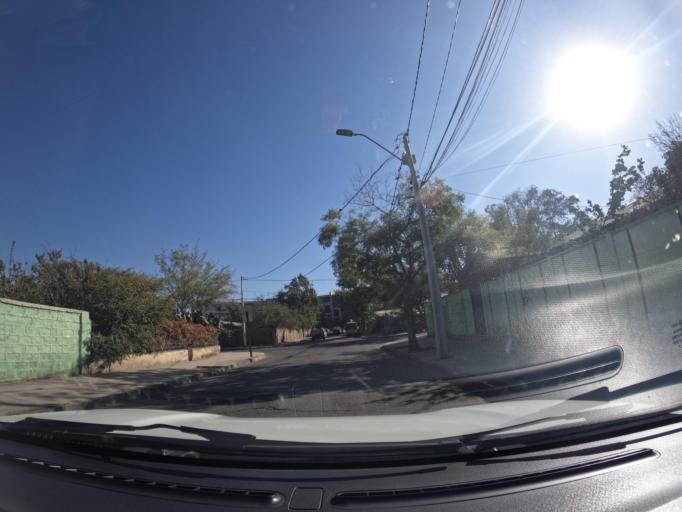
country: CL
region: Santiago Metropolitan
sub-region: Provincia de Santiago
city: Villa Presidente Frei, Nunoa, Santiago, Chile
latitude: -33.5089
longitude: -70.5800
